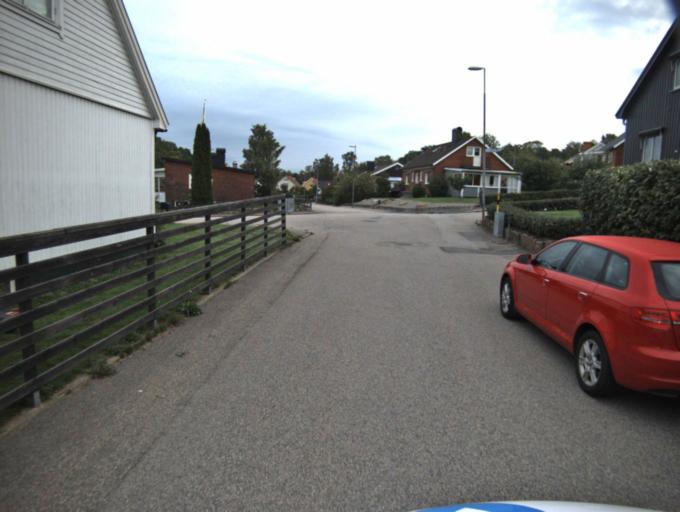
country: SE
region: Vaestra Goetaland
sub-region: Ulricehamns Kommun
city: Ulricehamn
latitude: 57.8009
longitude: 13.4295
